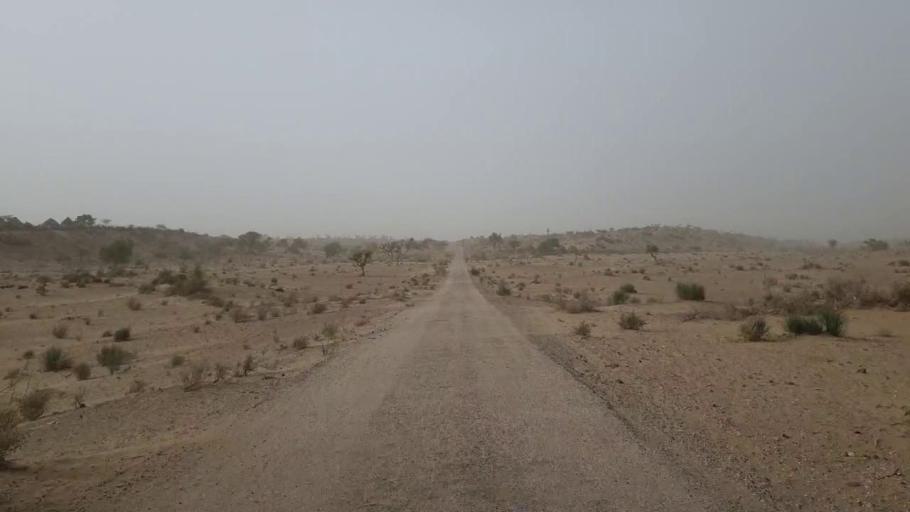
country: PK
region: Sindh
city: Islamkot
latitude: 24.5540
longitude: 70.3608
